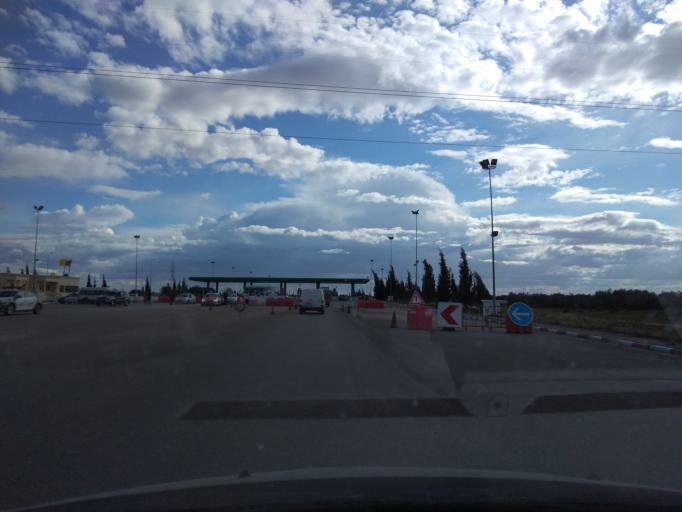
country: TN
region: Susah
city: Masakin
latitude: 35.6917
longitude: 10.5635
